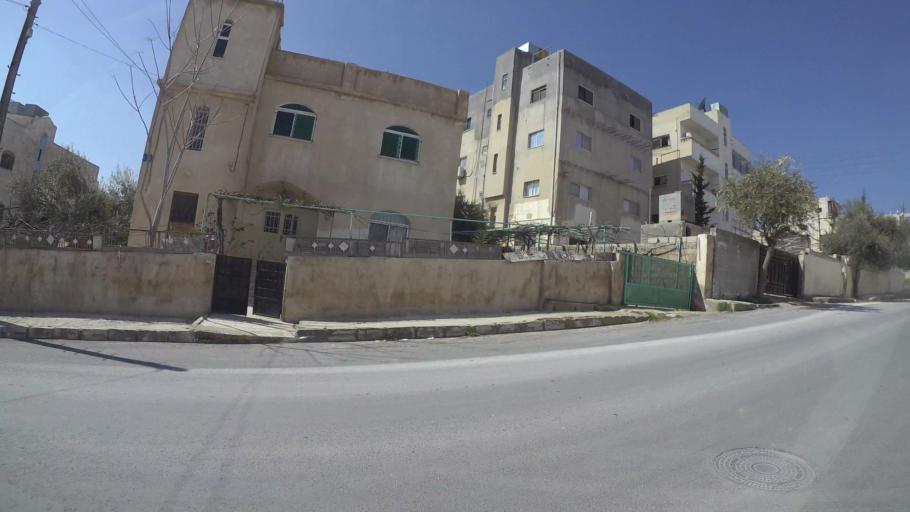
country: JO
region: Amman
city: Al Bunayyat ash Shamaliyah
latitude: 31.9038
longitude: 35.9055
